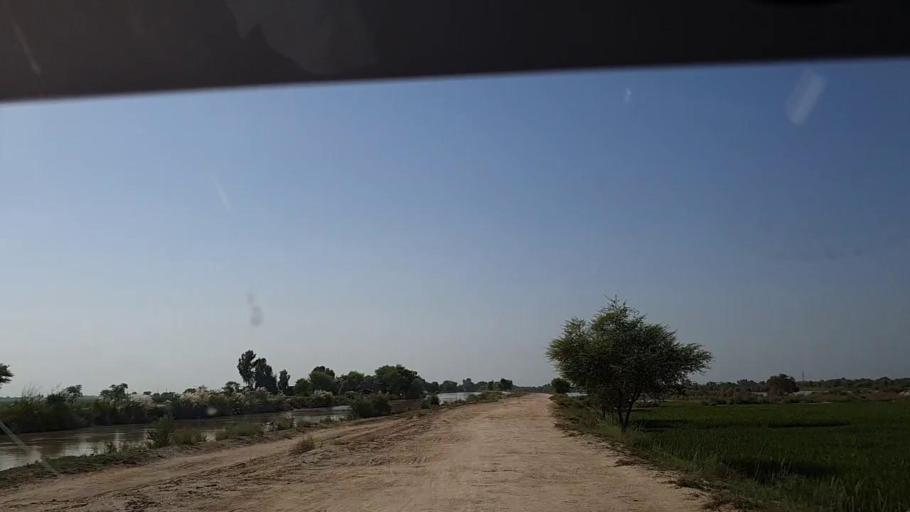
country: PK
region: Sindh
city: Ghauspur
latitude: 28.1773
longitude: 69.0929
